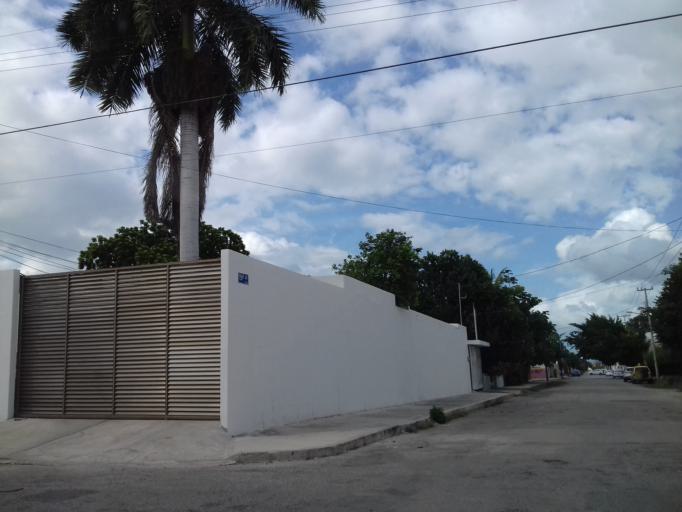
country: MX
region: Yucatan
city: Merida
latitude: 21.0010
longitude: -89.6137
